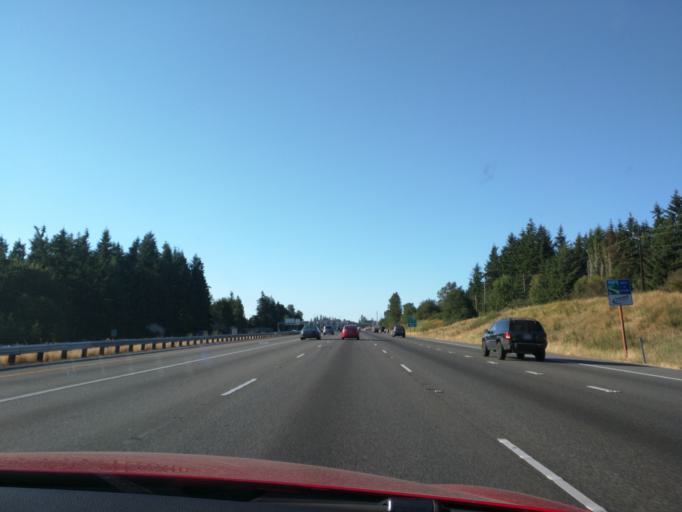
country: US
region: Washington
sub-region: Snohomish County
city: Martha Lake
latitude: 47.8404
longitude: -122.2597
